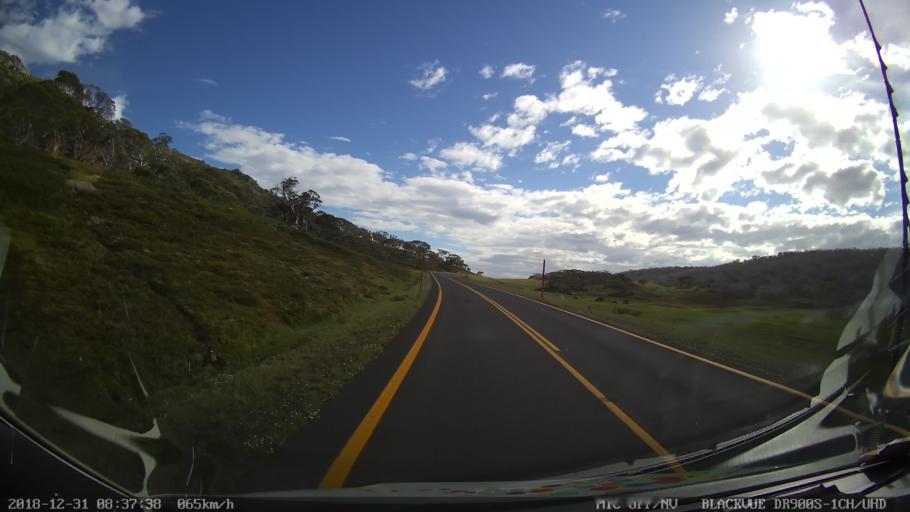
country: AU
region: New South Wales
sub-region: Snowy River
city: Jindabyne
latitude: -36.4184
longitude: 148.3874
